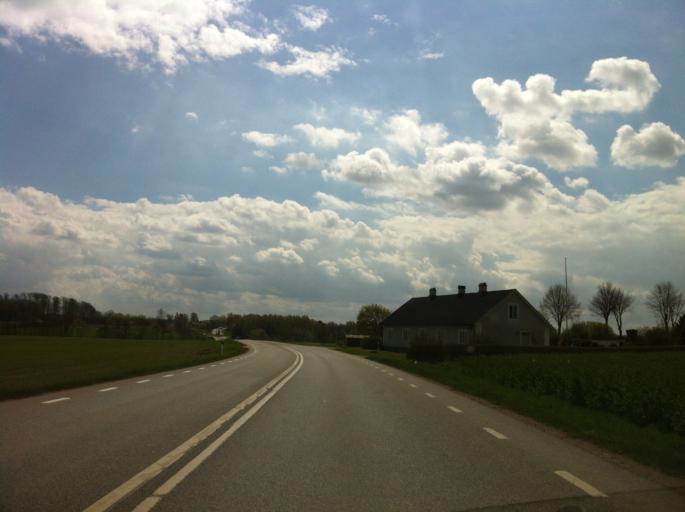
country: SE
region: Skane
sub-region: Hoors Kommun
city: Loberod
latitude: 55.8457
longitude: 13.4978
